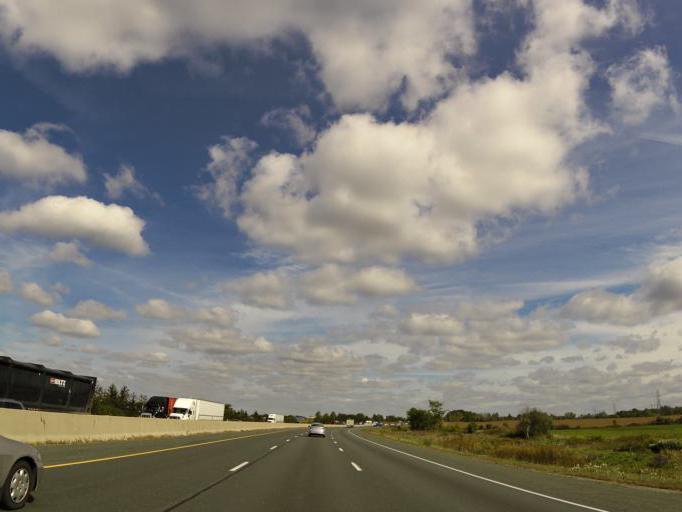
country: CA
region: Ontario
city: Dorchester
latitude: 42.9521
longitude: -81.0943
